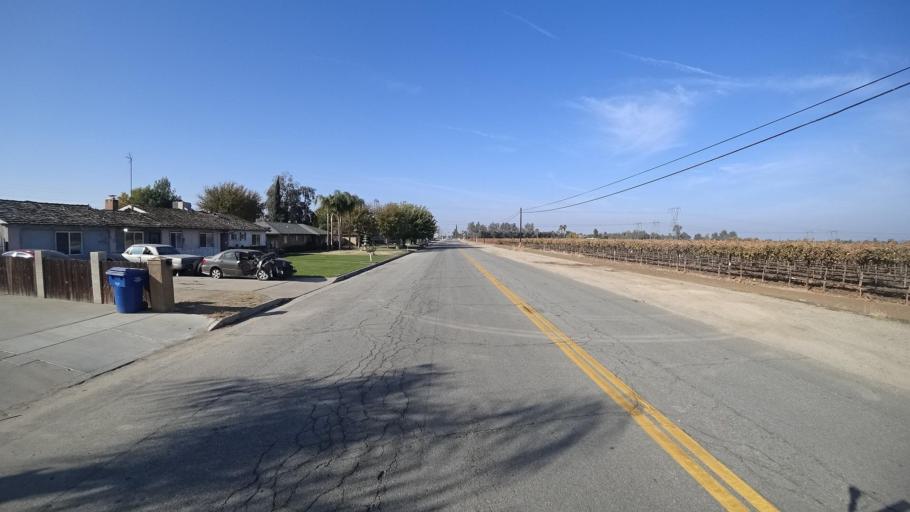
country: US
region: California
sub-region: Kern County
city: Lamont
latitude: 35.3398
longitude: -118.9202
